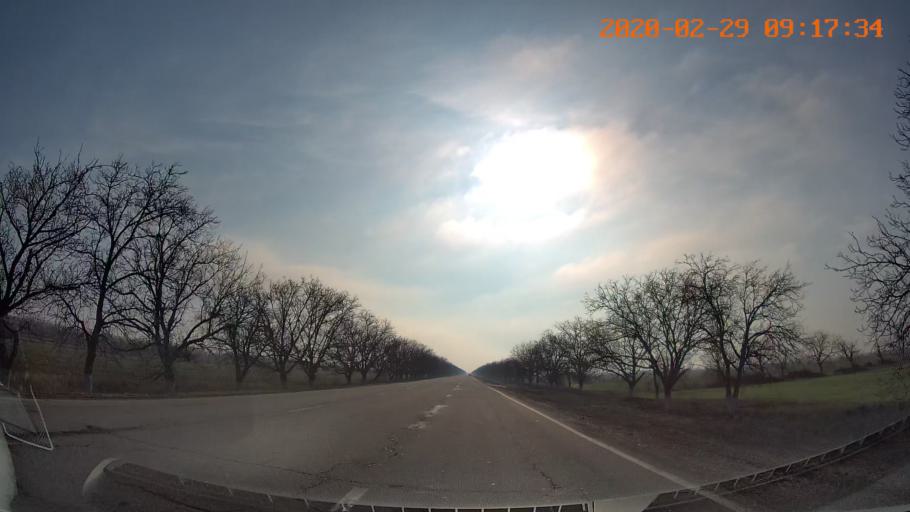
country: MD
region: Telenesti
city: Pervomaisc
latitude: 46.7817
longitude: 29.9067
